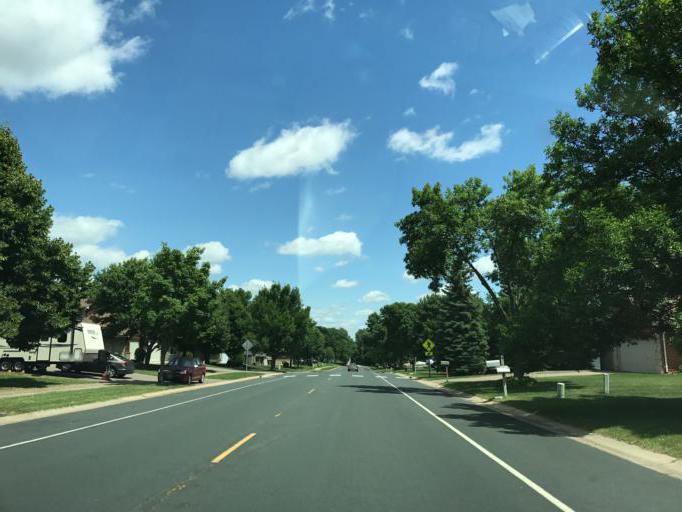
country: US
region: Minnesota
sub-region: Hennepin County
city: Maple Grove
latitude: 45.0813
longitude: -93.4236
